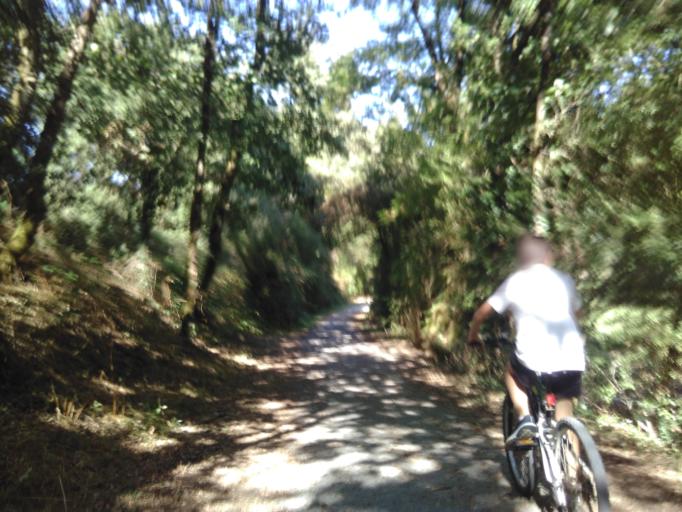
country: FR
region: Pays de la Loire
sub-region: Departement de la Vendee
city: La Chaize-le-Vicomte
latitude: 46.6639
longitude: -1.3018
